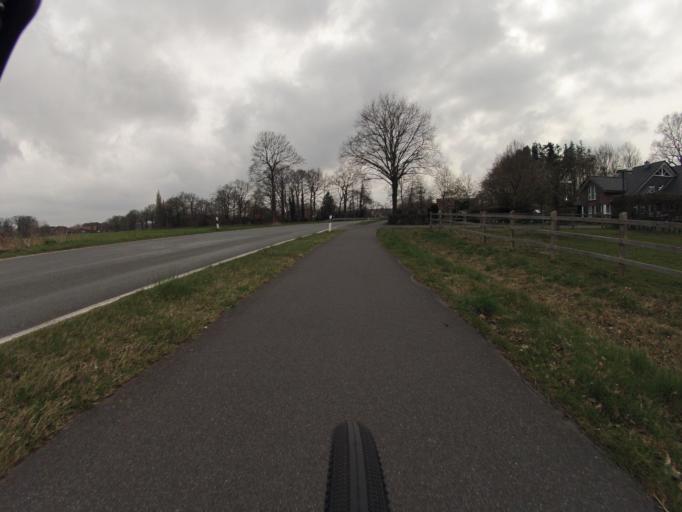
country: DE
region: North Rhine-Westphalia
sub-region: Regierungsbezirk Munster
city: Recke
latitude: 52.3526
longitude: 7.7156
